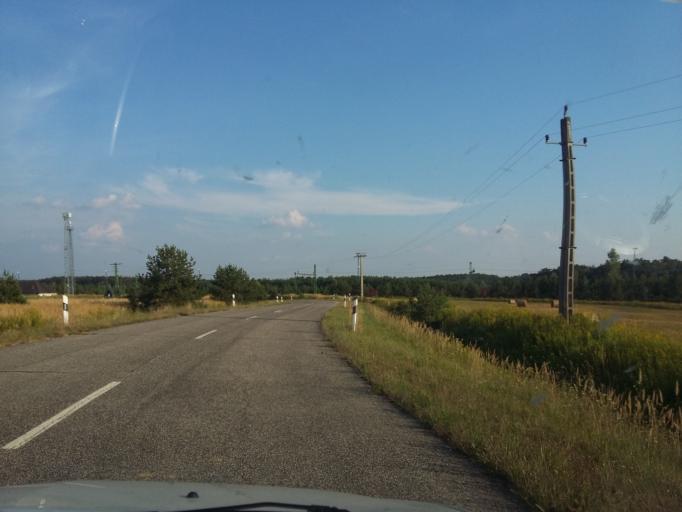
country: SI
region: Hodos-Hodos
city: Hodos
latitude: 46.8308
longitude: 16.4137
